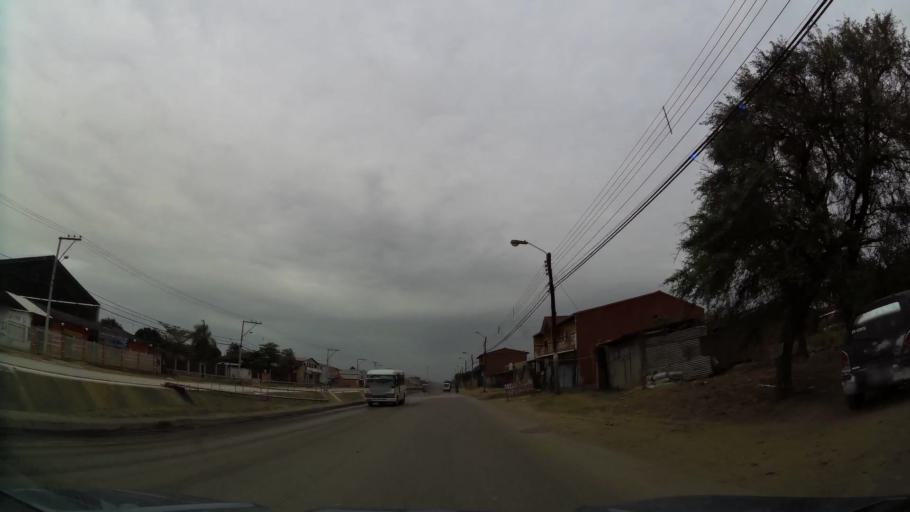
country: BO
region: Santa Cruz
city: Santa Cruz de la Sierra
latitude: -17.8572
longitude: -63.1769
